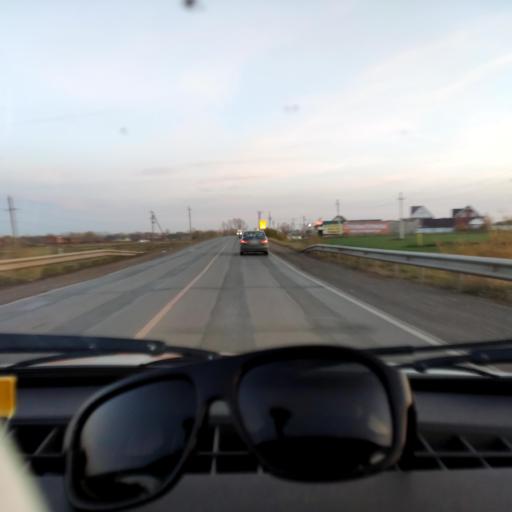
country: RU
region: Bashkortostan
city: Avdon
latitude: 54.7411
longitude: 55.7984
